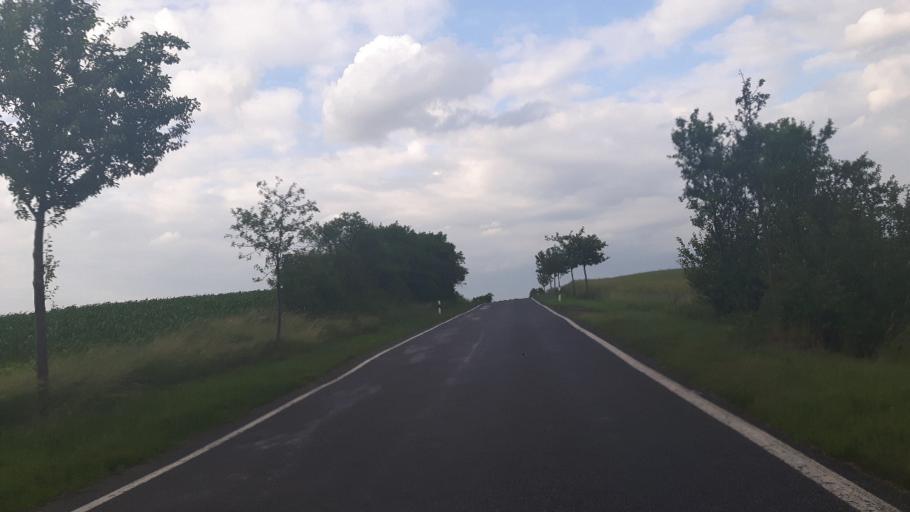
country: DE
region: Brandenburg
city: Hohenfinow
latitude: 52.8021
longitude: 13.9082
